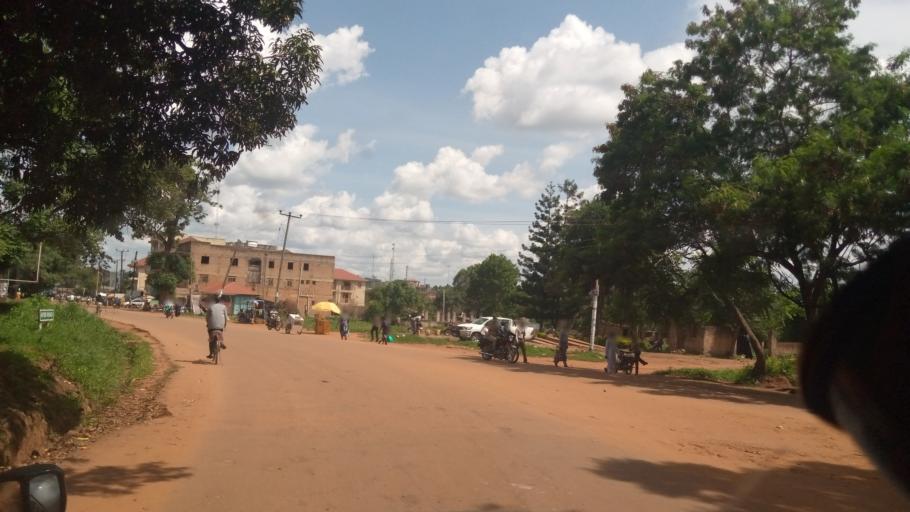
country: UG
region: Northern Region
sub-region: Lira District
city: Lira
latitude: 2.2491
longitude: 32.8985
